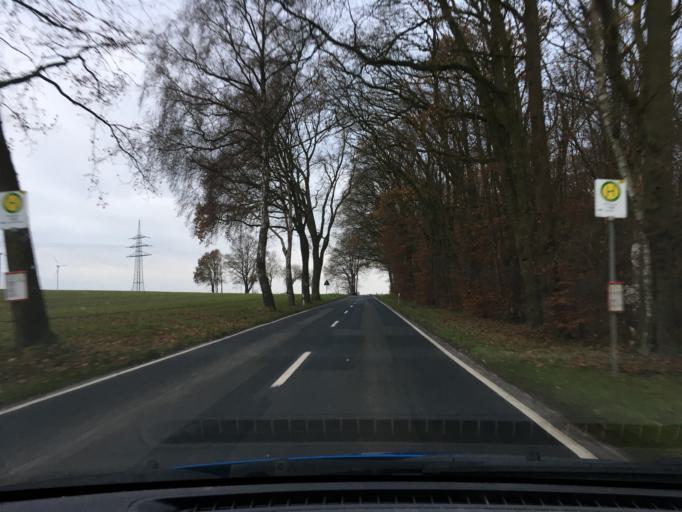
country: DE
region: Lower Saxony
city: Ebstorf
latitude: 52.9979
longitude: 10.4116
